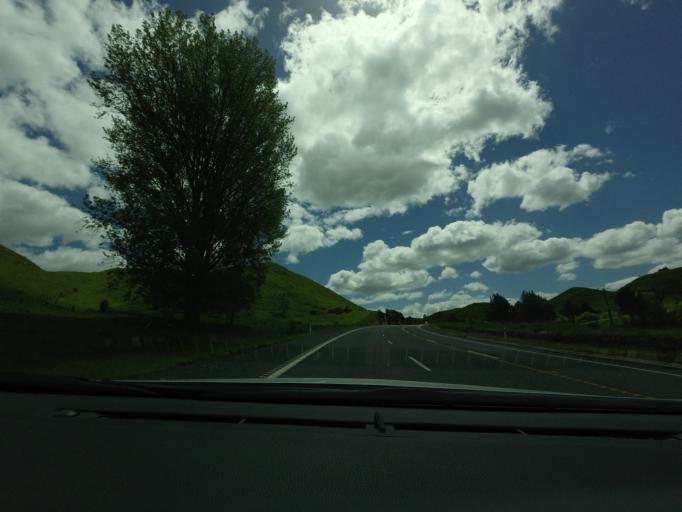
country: NZ
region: Bay of Plenty
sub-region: Rotorua District
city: Rotorua
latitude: -38.3024
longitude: 176.3661
